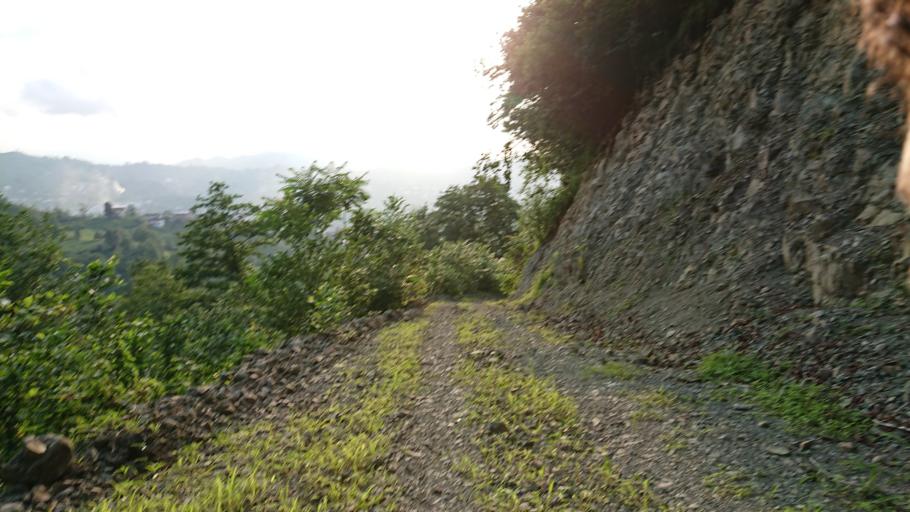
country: TR
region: Rize
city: Rize
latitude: 40.9907
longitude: 40.5025
